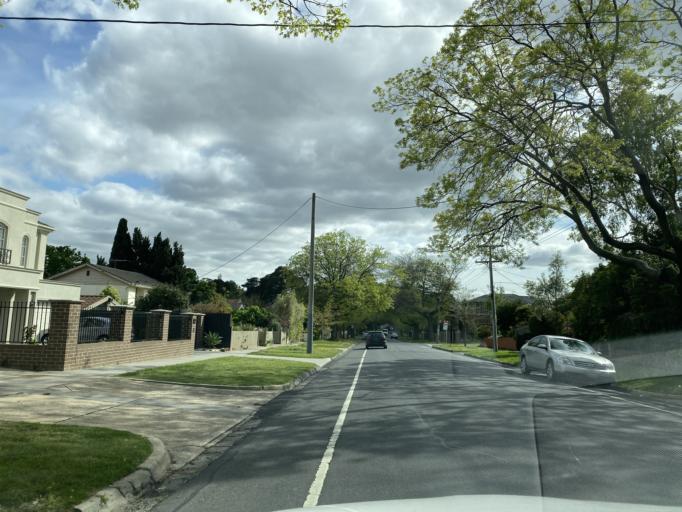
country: AU
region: Victoria
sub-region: Boroondara
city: Camberwell
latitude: -37.8476
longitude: 145.0824
